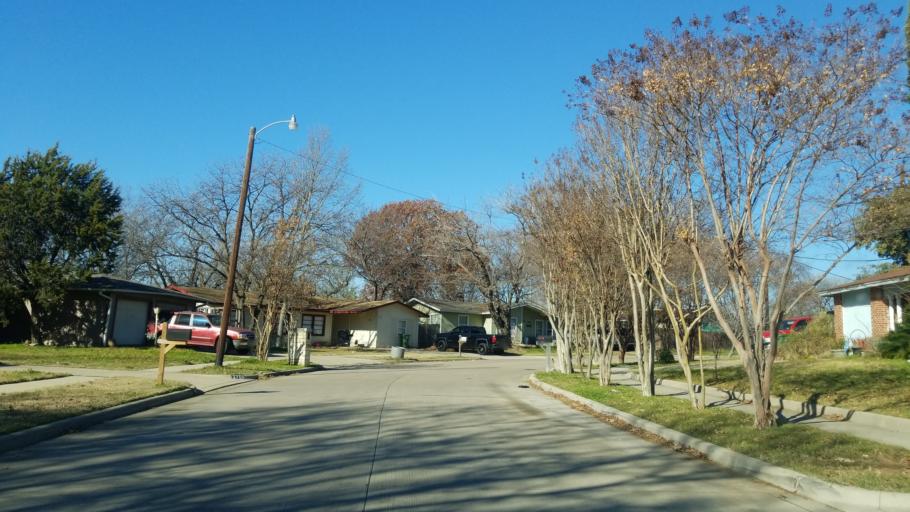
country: US
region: Texas
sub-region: Tarrant County
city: Arlington
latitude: 32.7291
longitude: -97.0608
